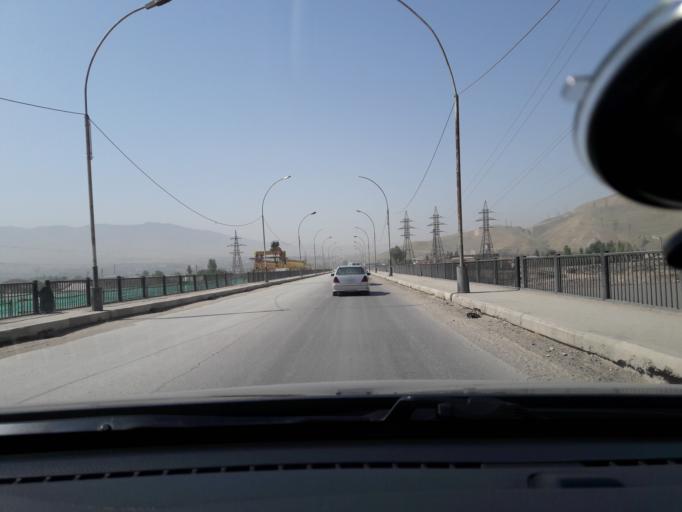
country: TJ
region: Dushanbe
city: Boshkengash
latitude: 38.4591
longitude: 68.7366
